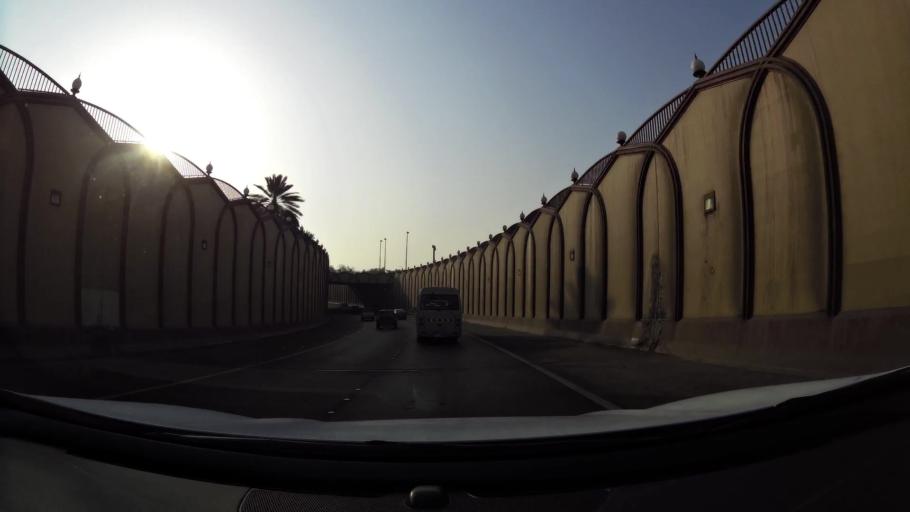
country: AE
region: Abu Dhabi
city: Abu Dhabi
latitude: 24.4190
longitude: 54.4746
